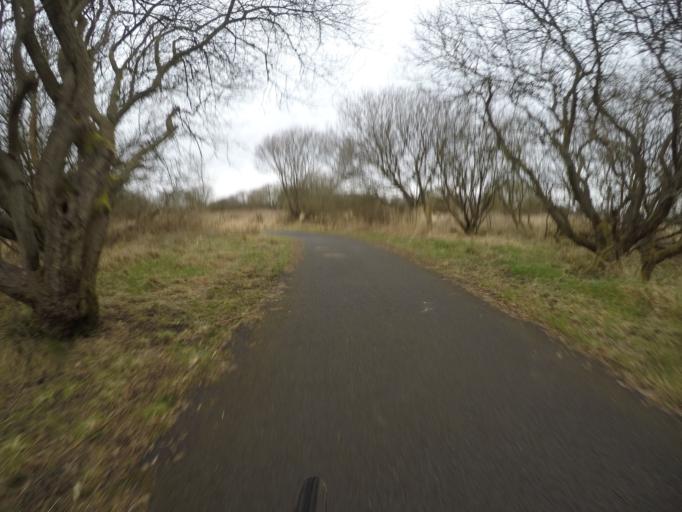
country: GB
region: Scotland
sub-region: North Ayrshire
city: Kilwinning
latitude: 55.6305
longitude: -4.6893
